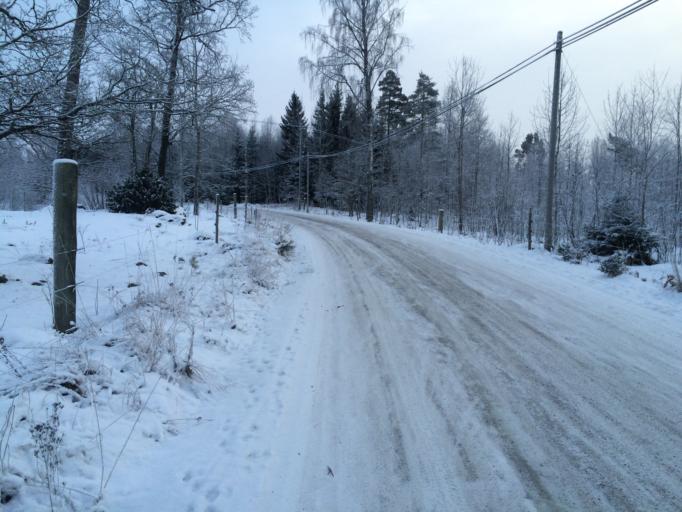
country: SE
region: Uppsala
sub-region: Enkopings Kommun
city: Orsundsbro
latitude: 59.9095
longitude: 17.1811
